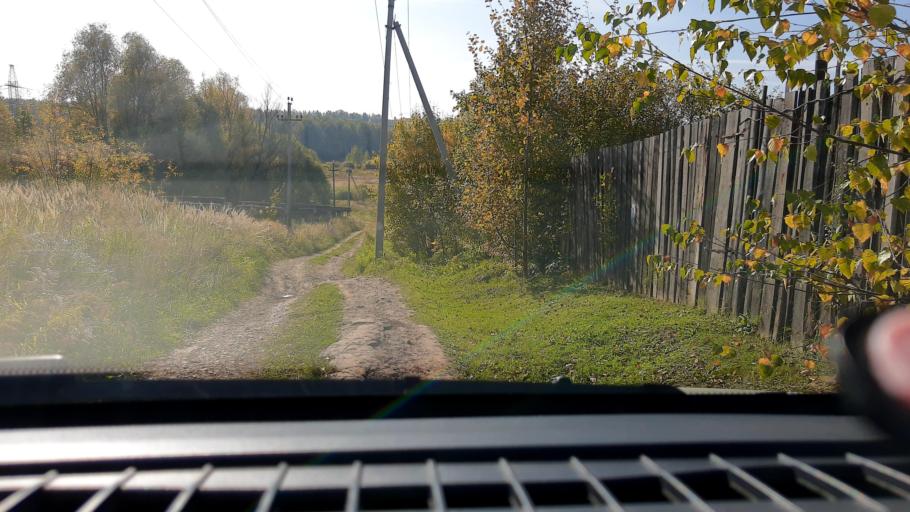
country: RU
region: Nizjnij Novgorod
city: Afonino
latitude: 56.2390
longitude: 44.0592
